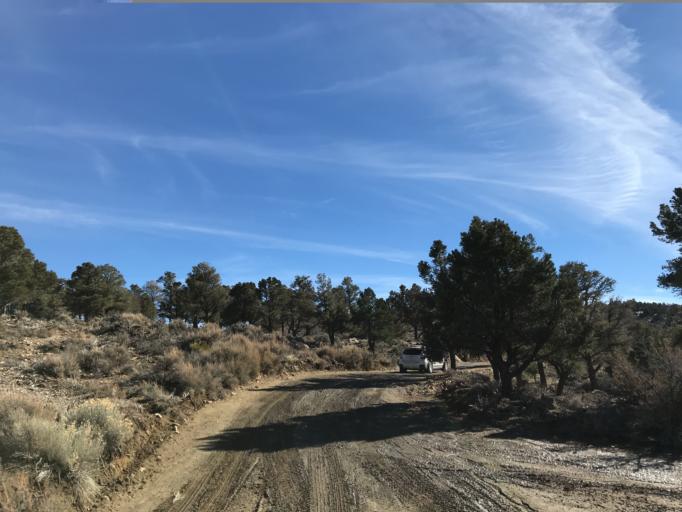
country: US
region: California
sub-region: San Bernardino County
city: Big Bear City
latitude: 34.2811
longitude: -116.7875
